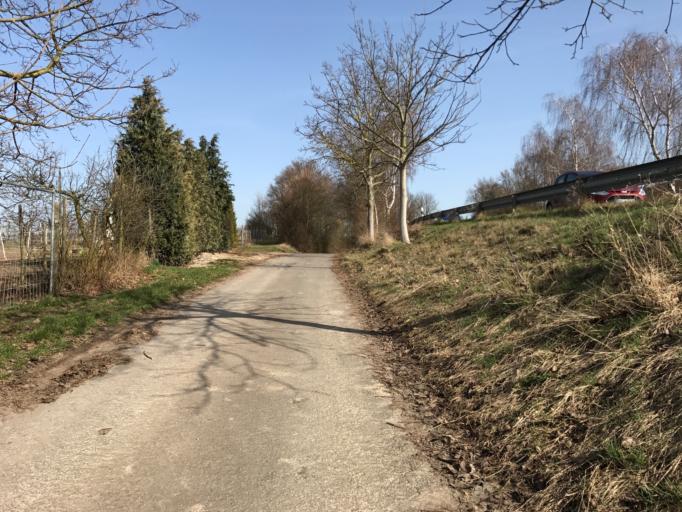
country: DE
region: Rheinland-Pfalz
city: Essenheim
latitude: 49.9326
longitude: 8.1520
